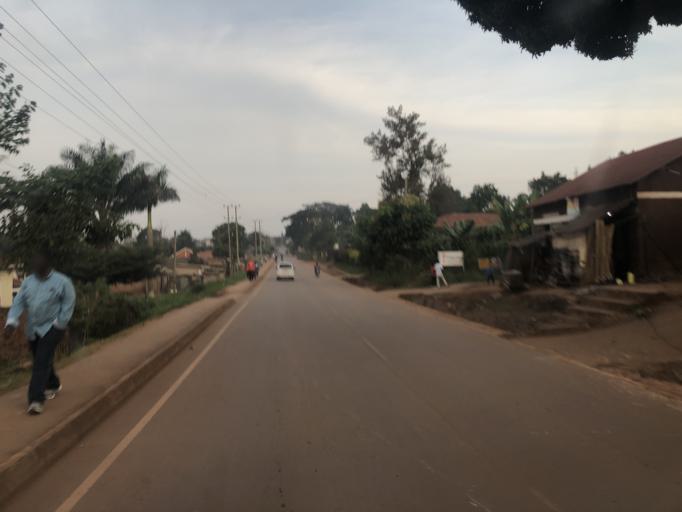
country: UG
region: Central Region
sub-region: Kampala District
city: Kampala
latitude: 0.2791
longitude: 32.5414
